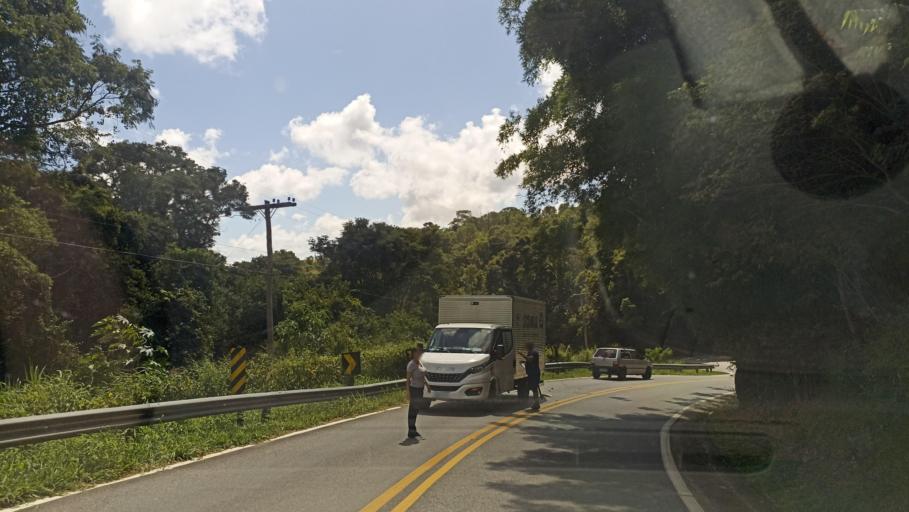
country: BR
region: Sao Paulo
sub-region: Cunha
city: Cunha
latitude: -23.1322
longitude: -44.9291
